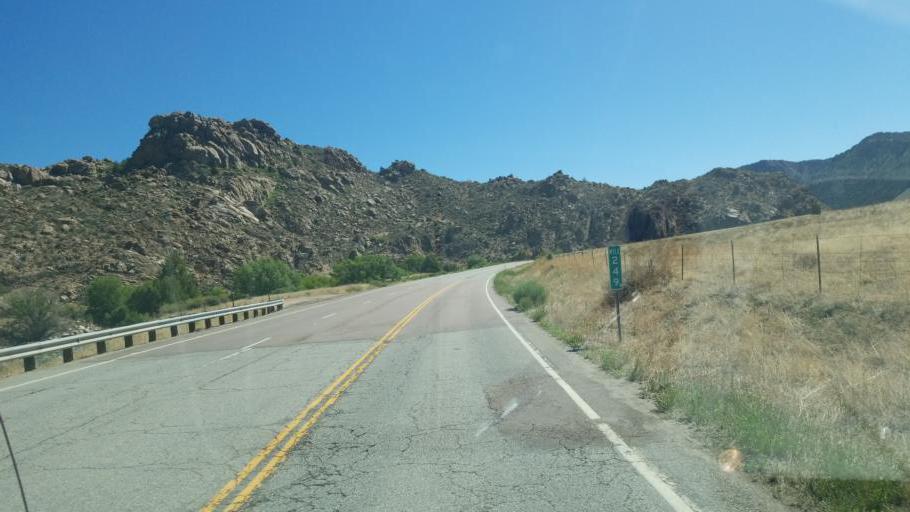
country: US
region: Colorado
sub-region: Custer County
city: Westcliffe
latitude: 38.3944
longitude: -105.6356
